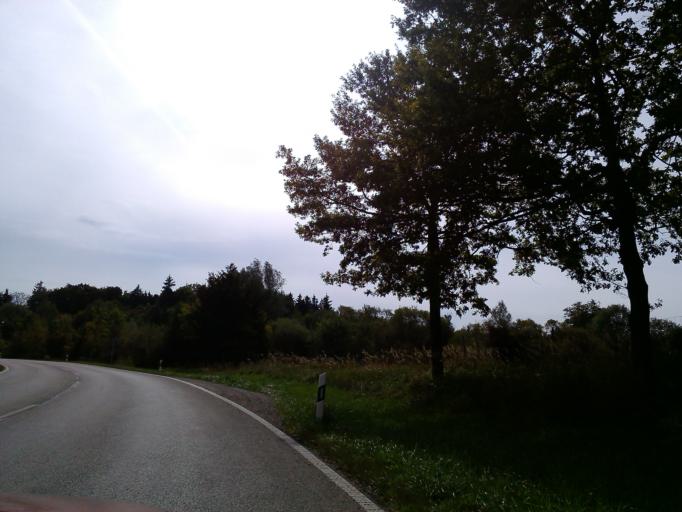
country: DE
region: Bavaria
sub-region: Upper Bavaria
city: Pocking
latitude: 47.9978
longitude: 11.2981
